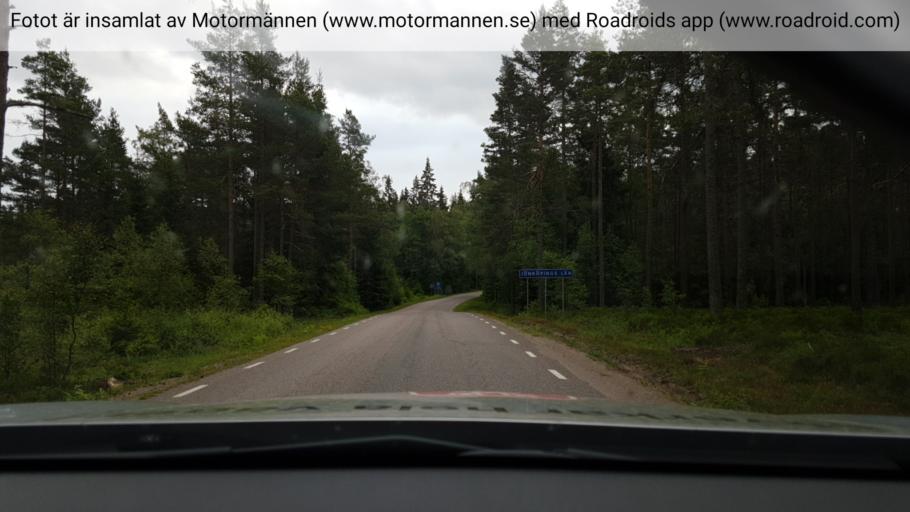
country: SE
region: Joenkoeping
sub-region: Habo Kommun
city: Habo
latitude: 58.0140
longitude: 14.0051
